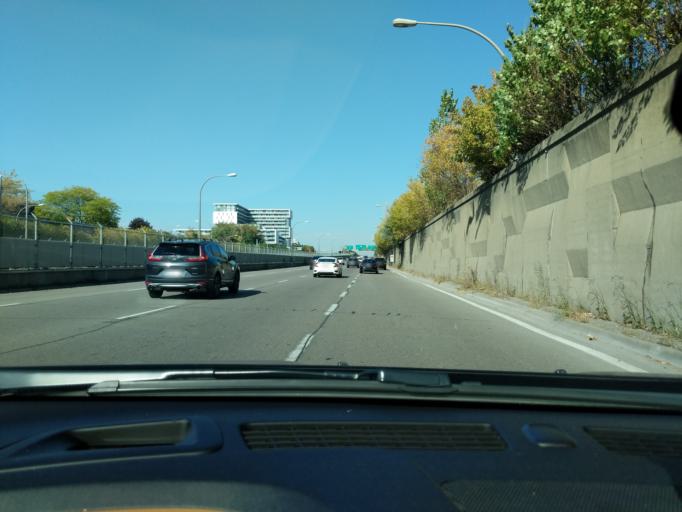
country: CA
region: Ontario
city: Toronto
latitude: 43.7195
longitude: -79.4452
